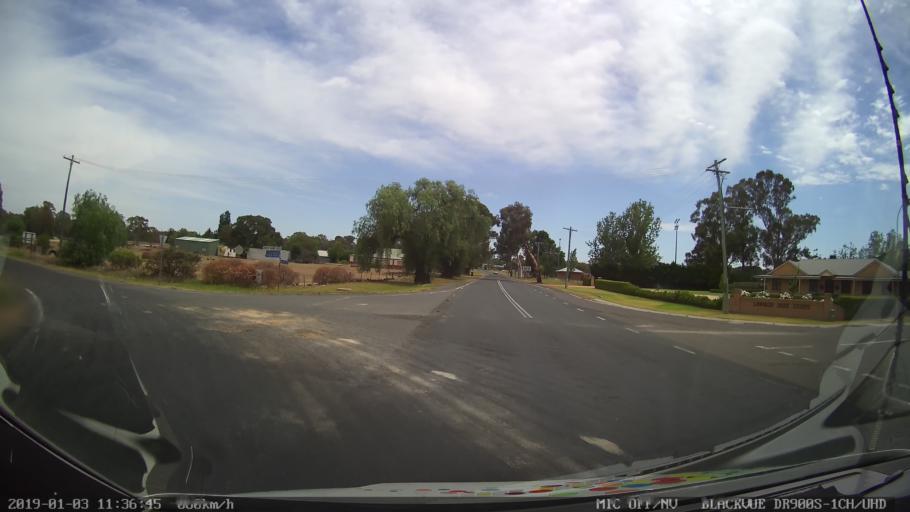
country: AU
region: New South Wales
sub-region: Weddin
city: Grenfell
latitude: -33.9076
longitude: 148.1600
